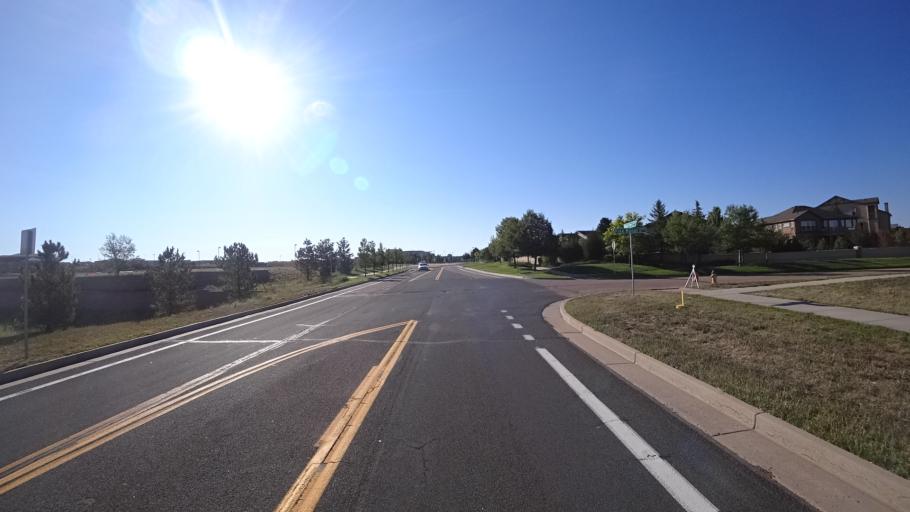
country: US
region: Colorado
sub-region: El Paso County
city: Black Forest
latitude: 38.9728
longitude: -104.7550
